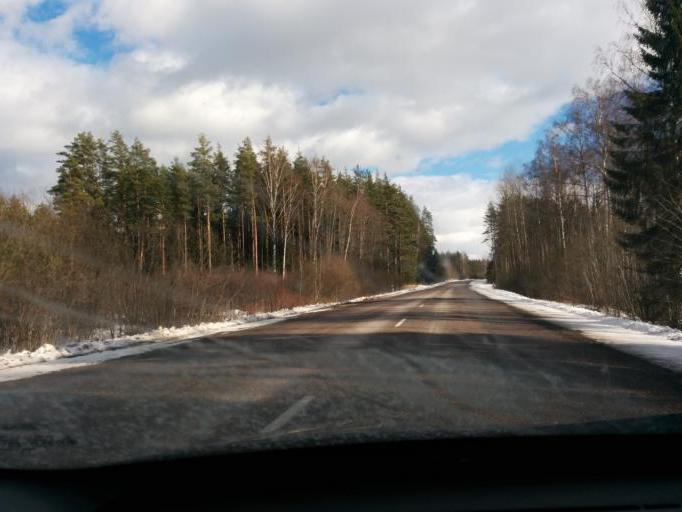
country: LV
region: Gulbenes Rajons
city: Gulbene
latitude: 57.2295
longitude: 26.5299
